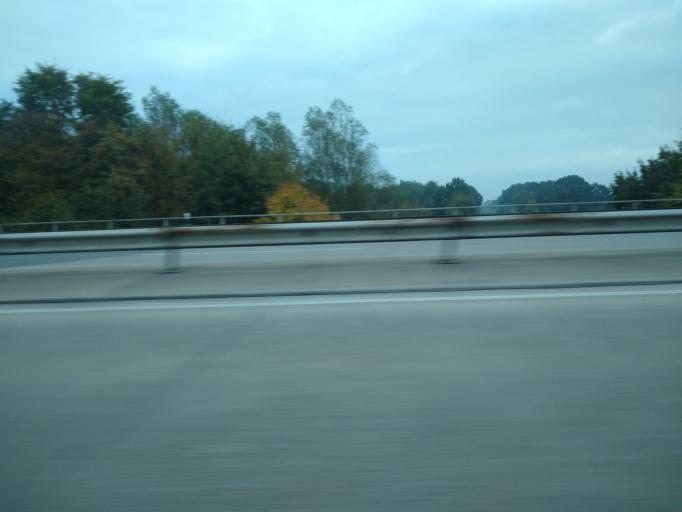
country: DE
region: Lower Saxony
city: Oldenburg
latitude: 53.1278
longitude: 8.2756
